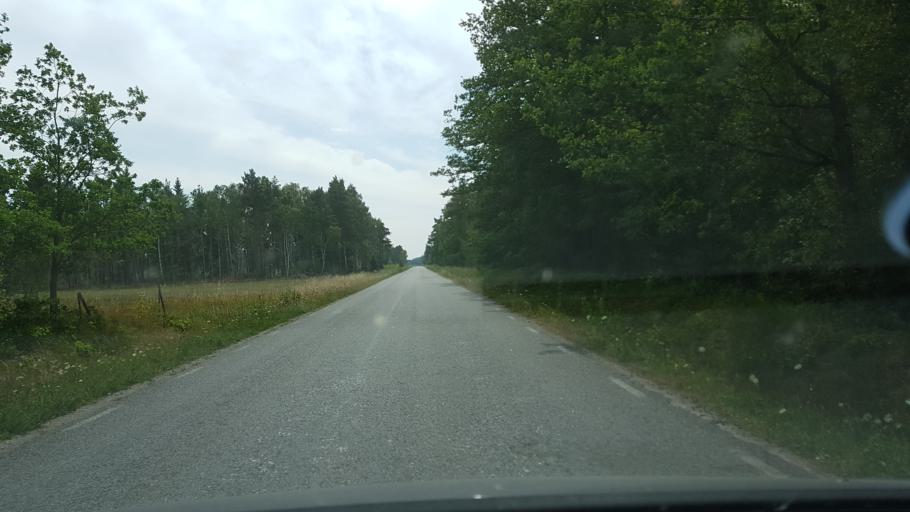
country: SE
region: Gotland
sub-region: Gotland
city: Visby
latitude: 57.7150
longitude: 18.5088
